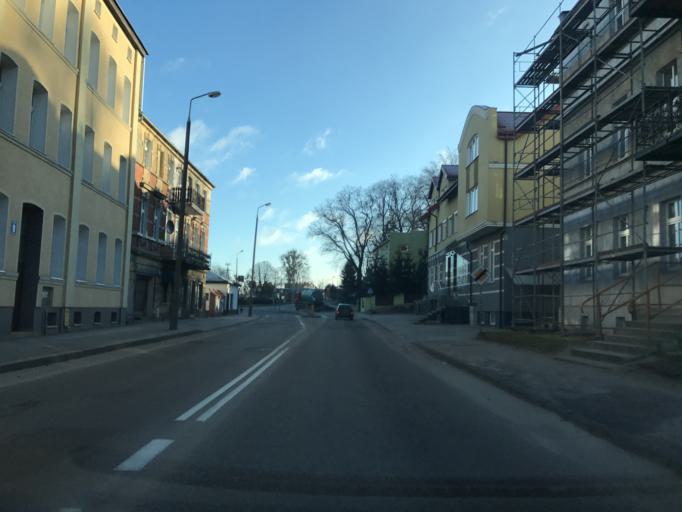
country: PL
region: Warmian-Masurian Voivodeship
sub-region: Powiat ostrodzki
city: Ostroda
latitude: 53.7003
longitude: 19.9566
